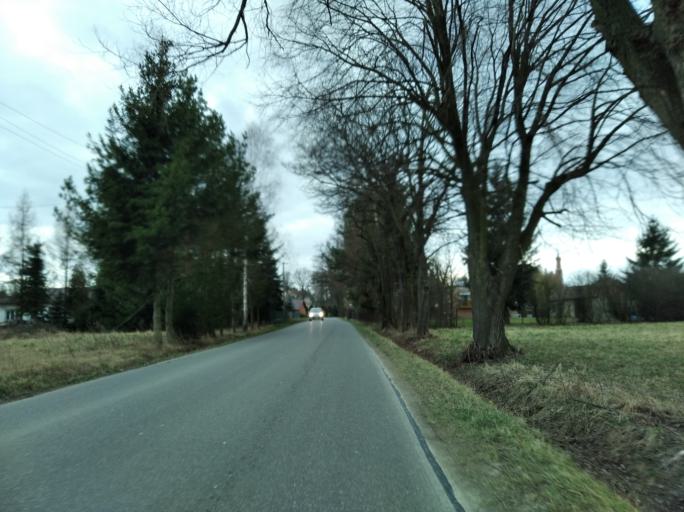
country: PL
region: Subcarpathian Voivodeship
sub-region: Powiat krosnienski
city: Odrzykon
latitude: 49.7490
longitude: 21.7044
